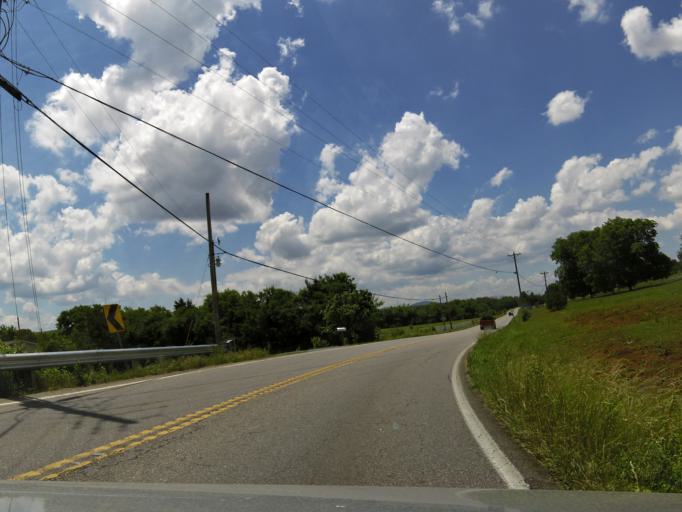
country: US
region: Tennessee
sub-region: Blount County
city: Maryville
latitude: 35.6854
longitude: -84.0388
